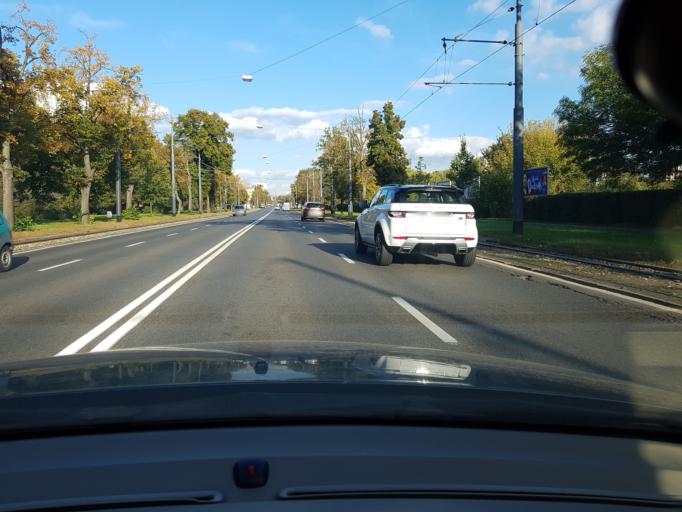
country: PL
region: Masovian Voivodeship
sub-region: Warszawa
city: Praga Poludnie
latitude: 52.2413
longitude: 21.0670
